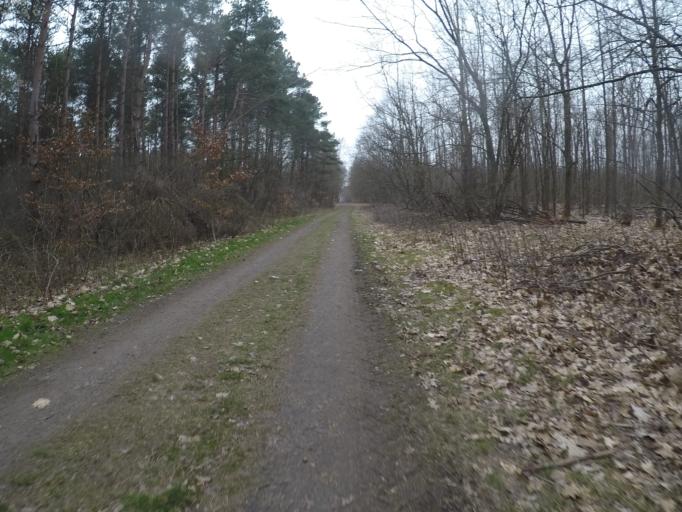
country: DE
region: Lower Saxony
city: Cuxhaven
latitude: 53.8296
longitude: 8.6449
